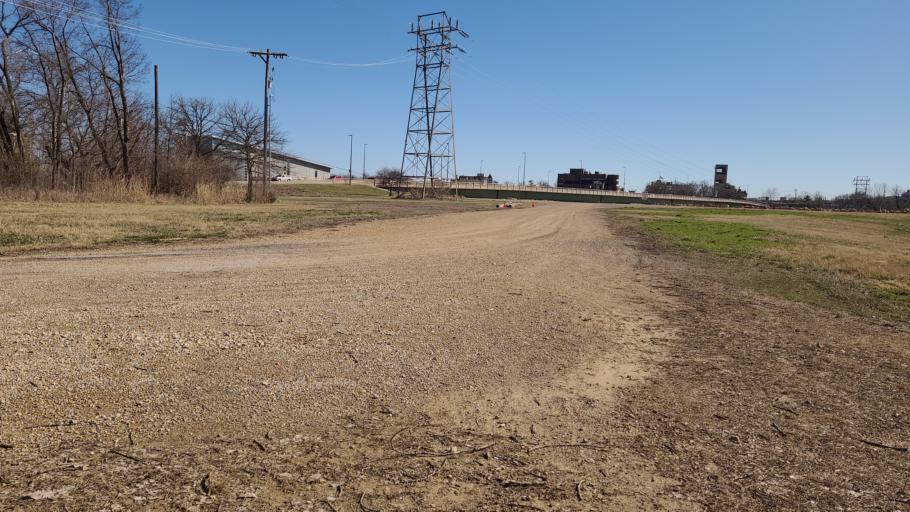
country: US
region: Kansas
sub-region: Douglas County
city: Lawrence
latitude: 38.9778
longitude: -95.2363
